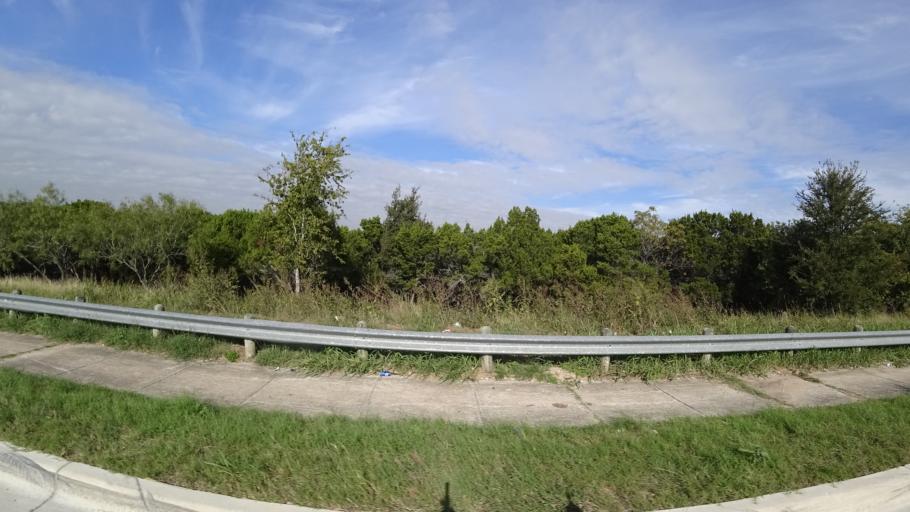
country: US
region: Texas
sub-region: Travis County
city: Austin
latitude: 30.2008
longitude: -97.7221
